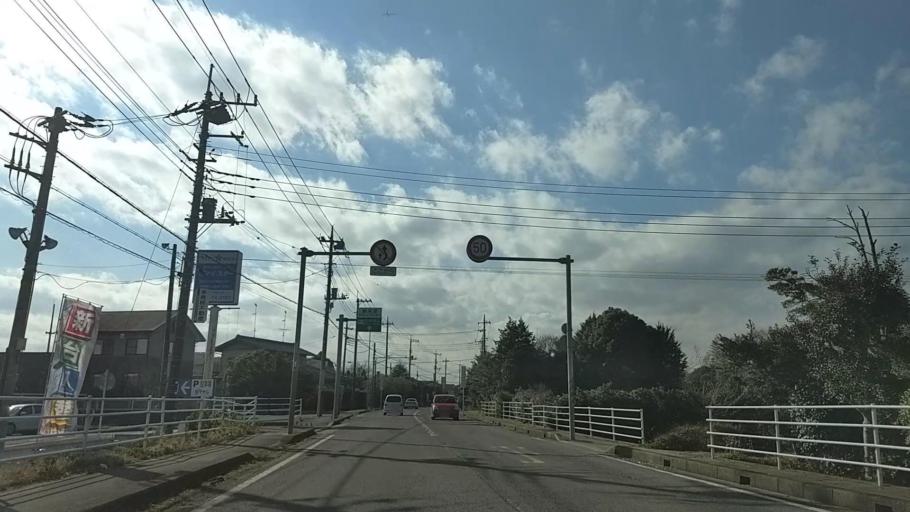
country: JP
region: Chiba
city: Yokaichiba
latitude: 35.6587
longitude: 140.4823
